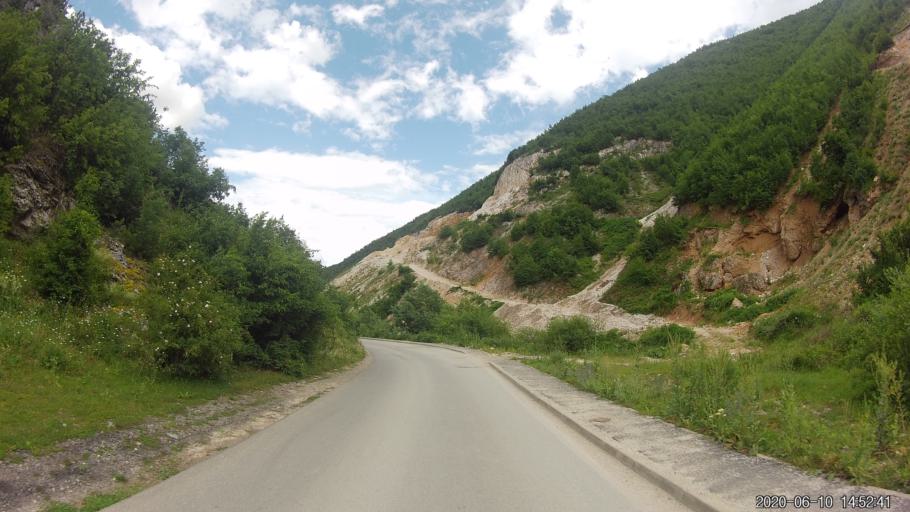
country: XK
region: Ferizaj
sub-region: Komuna e Shtimes
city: Shtime
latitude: 42.4012
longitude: 20.9845
